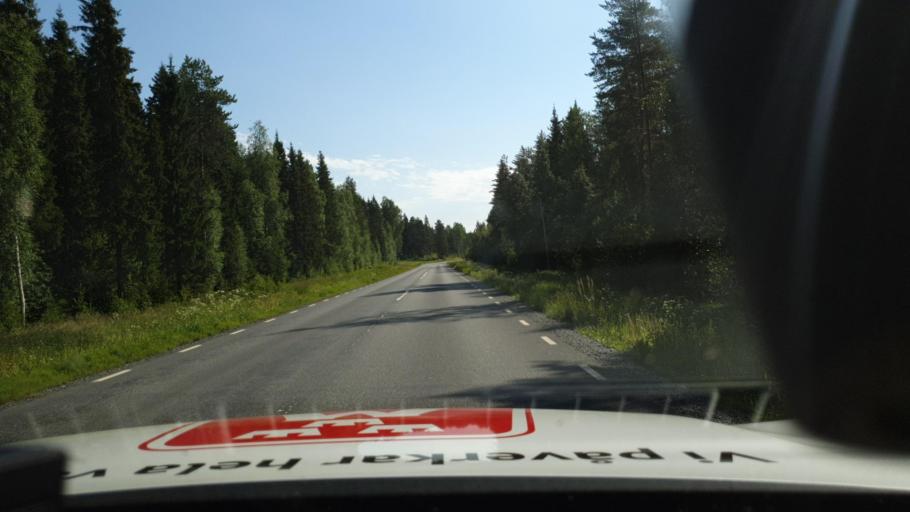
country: SE
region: Norrbotten
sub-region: Lulea Kommun
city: Ranea
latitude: 65.7905
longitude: 22.1212
